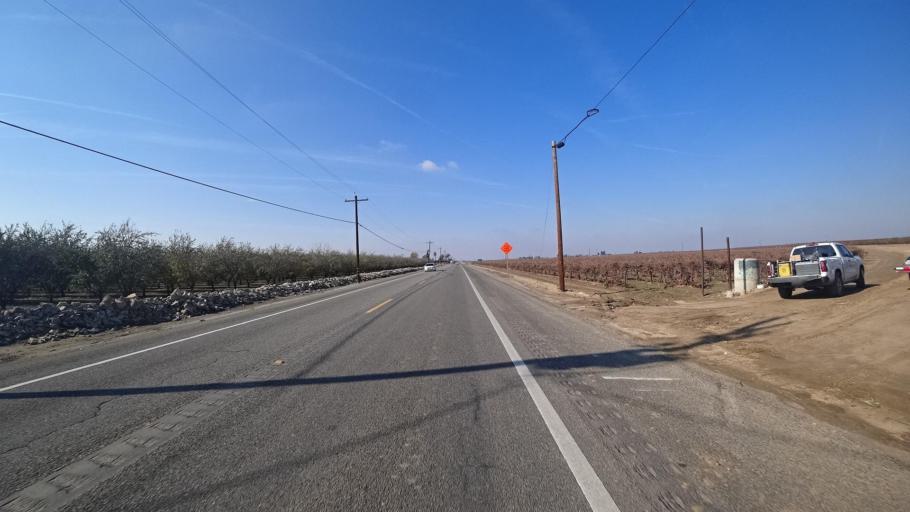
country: US
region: California
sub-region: Kern County
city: Arvin
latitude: 35.2089
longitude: -118.8655
